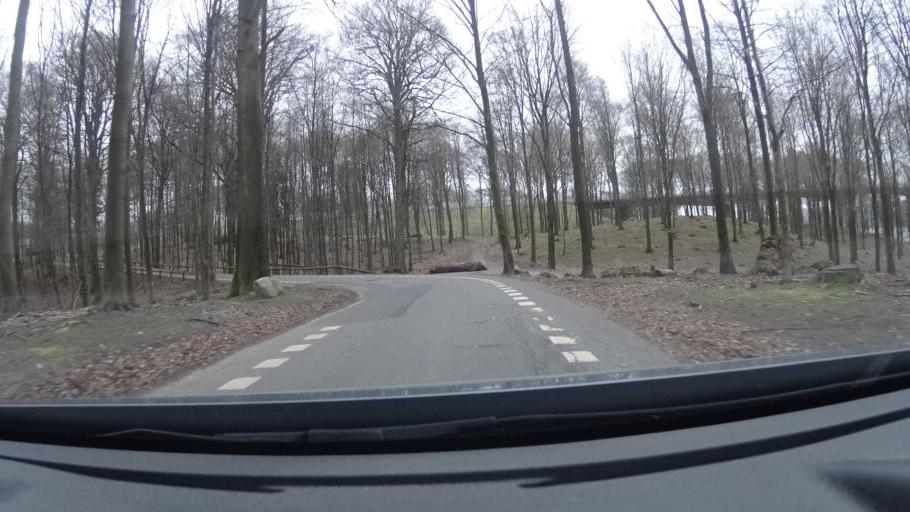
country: DK
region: South Denmark
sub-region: Vejle Kommune
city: Vejle
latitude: 55.7085
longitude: 9.5722
